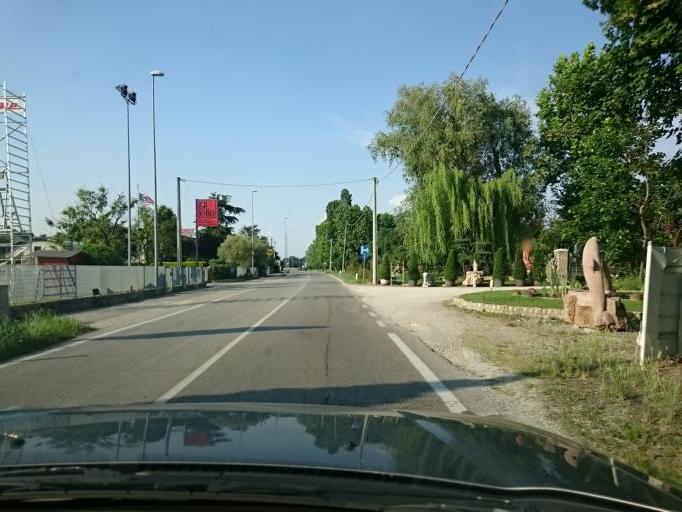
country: IT
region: Veneto
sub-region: Provincia di Padova
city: Abano Terme
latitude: 45.3471
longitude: 11.8025
